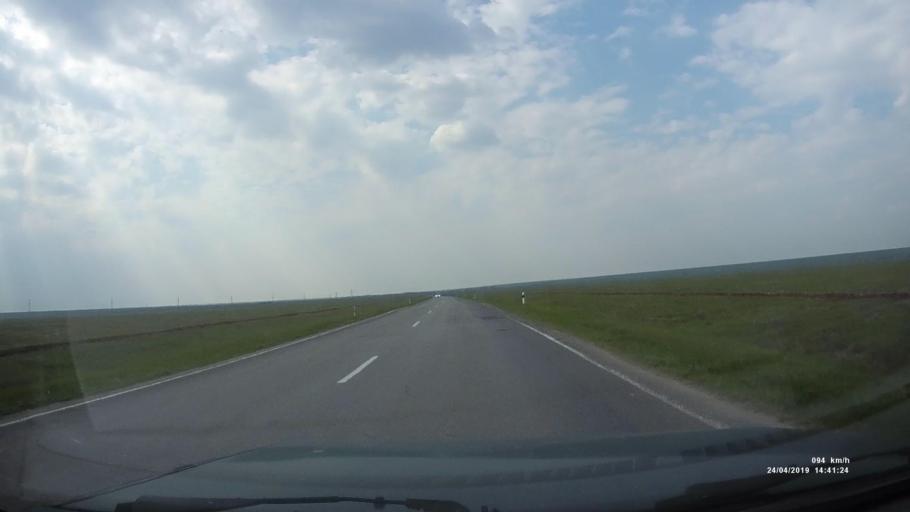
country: RU
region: Rostov
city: Remontnoye
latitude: 46.4450
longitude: 43.8799
